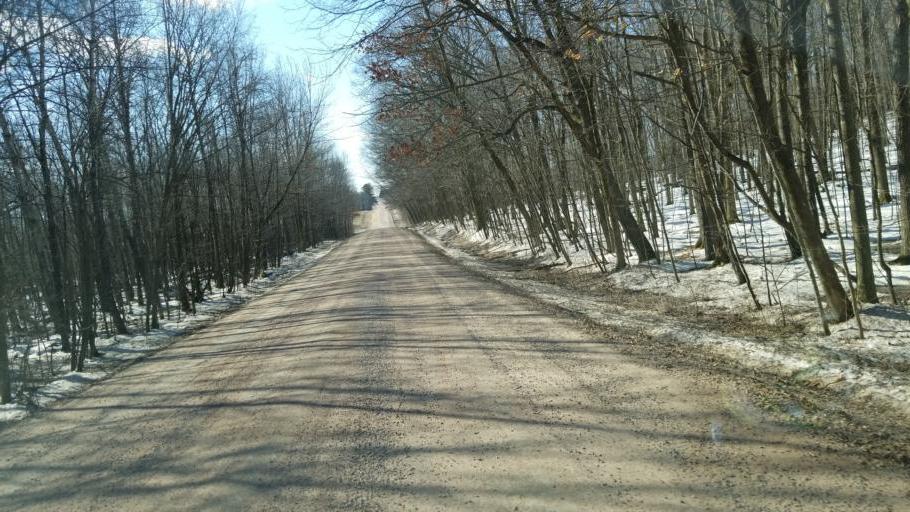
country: US
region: Wisconsin
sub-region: Clark County
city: Loyal
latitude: 44.6609
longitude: -90.4559
